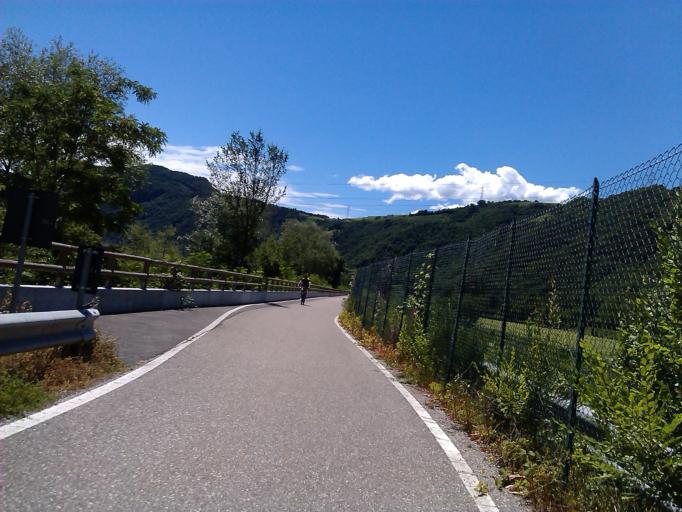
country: IT
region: Trentino-Alto Adige
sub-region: Bolzano
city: Cornaiano
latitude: 46.4704
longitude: 11.3080
